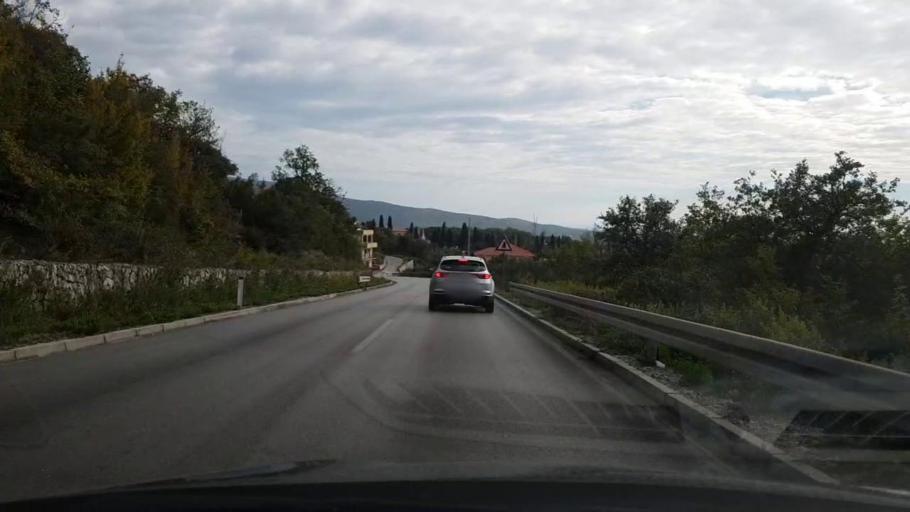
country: ME
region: Herceg Novi
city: Herceg-Novi
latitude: 42.4655
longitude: 18.5447
